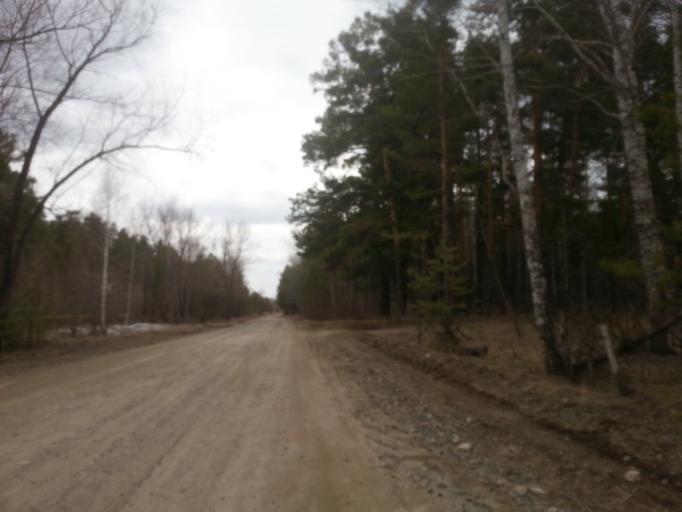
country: RU
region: Altai Krai
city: Yuzhnyy
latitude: 53.2808
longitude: 83.7345
